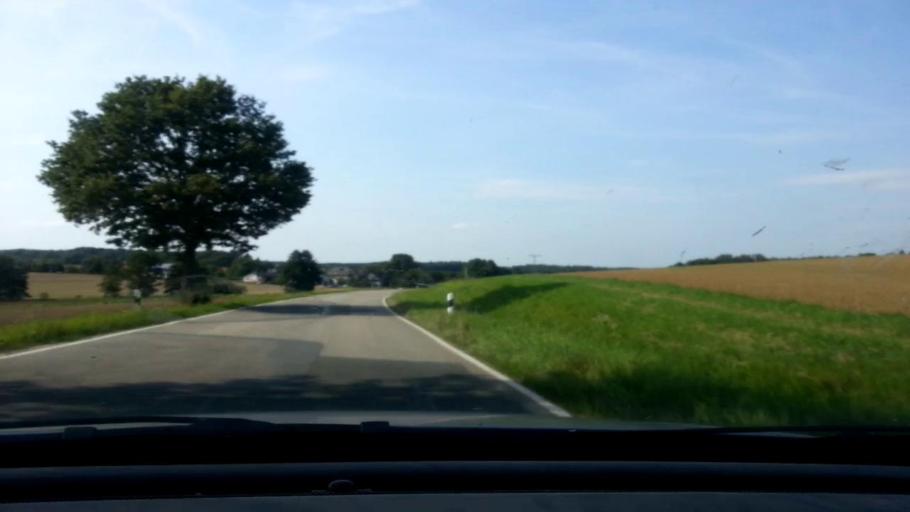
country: DE
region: Bavaria
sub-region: Upper Franconia
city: Schesslitz
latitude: 49.9690
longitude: 10.9904
